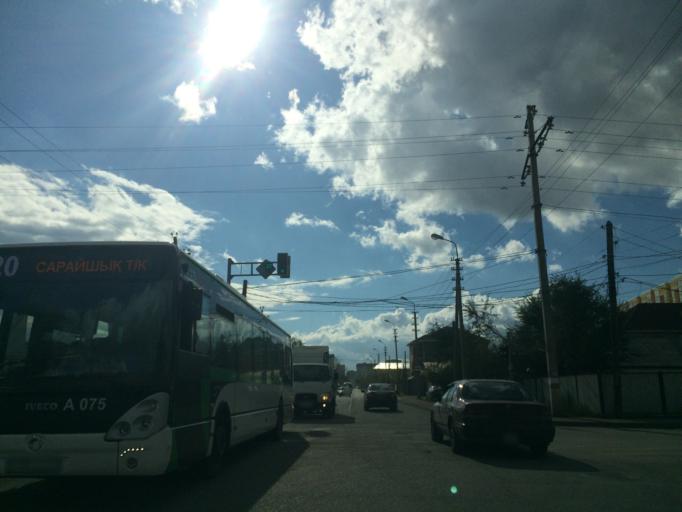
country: KZ
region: Astana Qalasy
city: Astana
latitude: 51.1904
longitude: 71.3862
